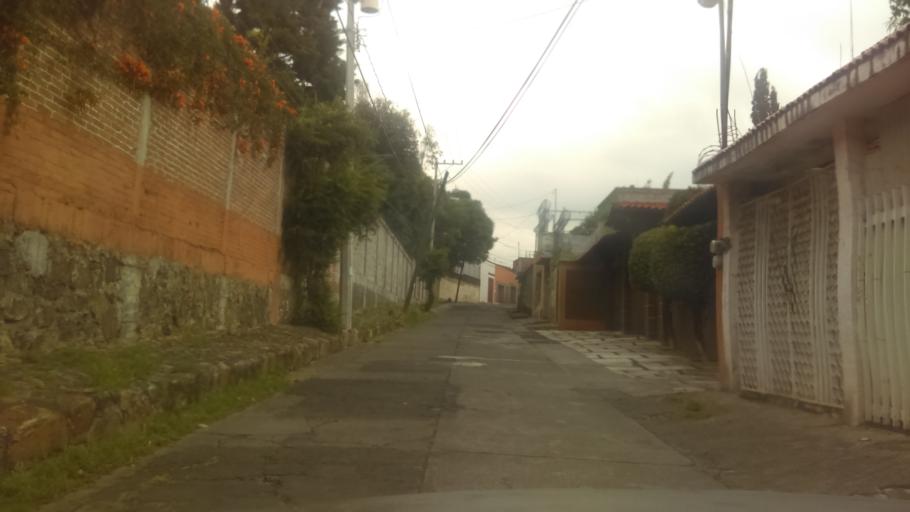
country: MX
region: Michoacan
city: Morelia
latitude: 19.6726
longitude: -101.1938
